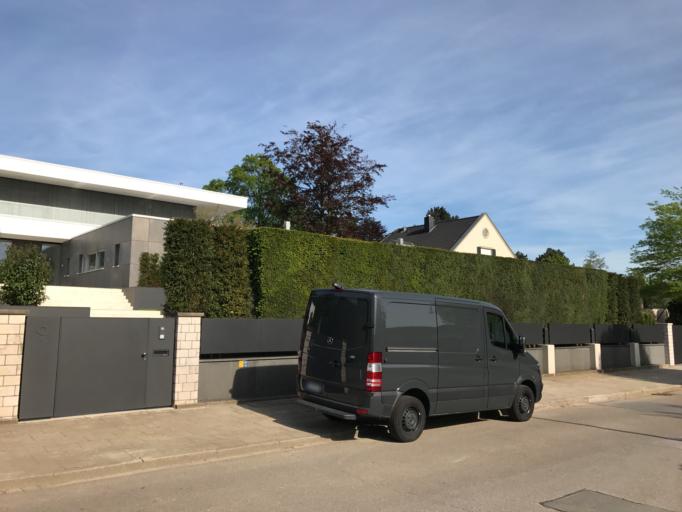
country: DE
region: North Rhine-Westphalia
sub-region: Regierungsbezirk Dusseldorf
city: Essen
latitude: 51.4026
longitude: 6.9796
